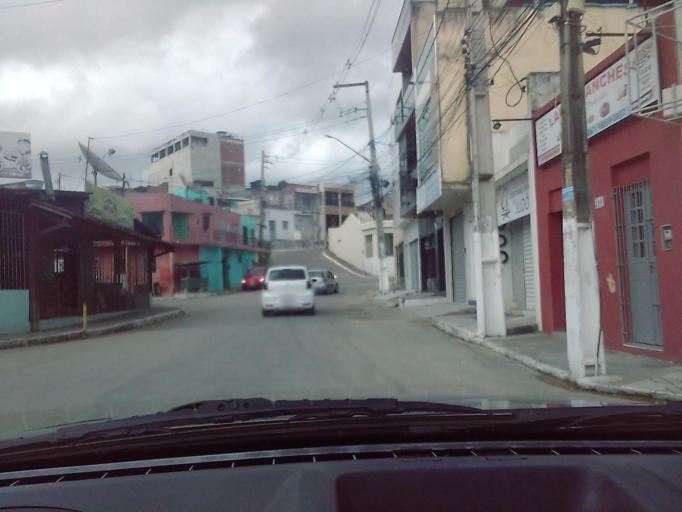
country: BR
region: Pernambuco
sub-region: Vitoria De Santo Antao
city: Vitoria de Santo Antao
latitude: -8.1234
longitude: -35.2961
